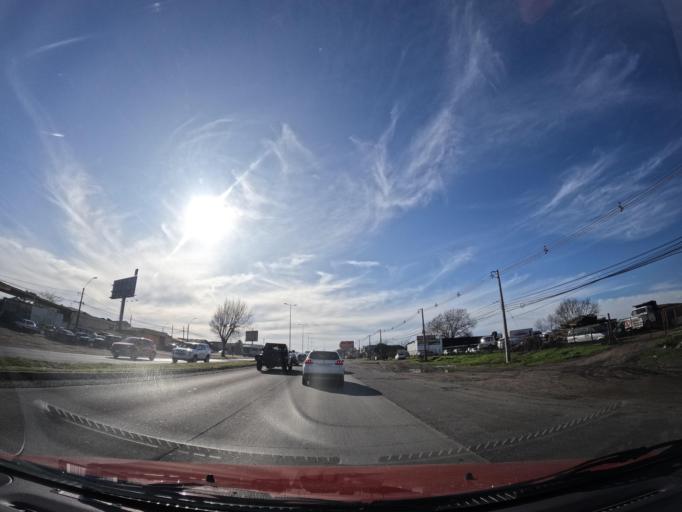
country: CL
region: Biobio
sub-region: Provincia de Concepcion
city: Talcahuano
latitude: -36.7731
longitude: -73.0814
